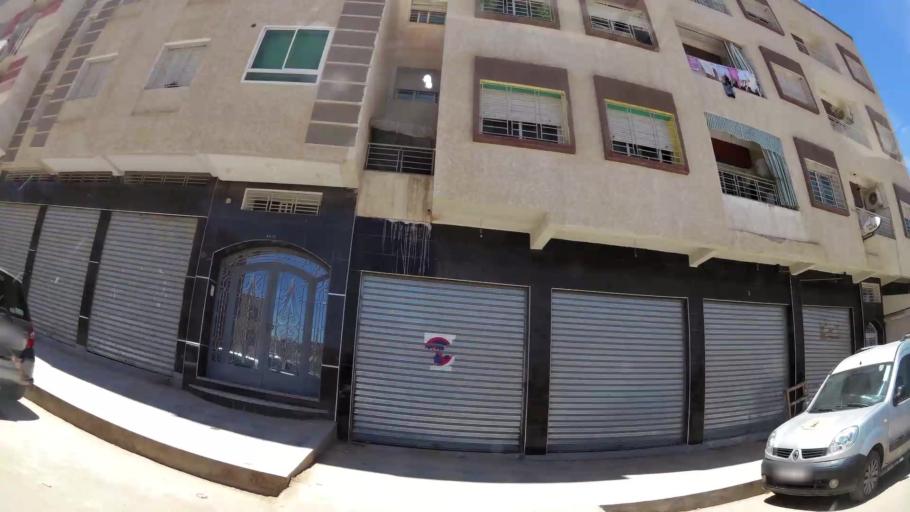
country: MA
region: Meknes-Tafilalet
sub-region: Meknes
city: Meknes
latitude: 33.8577
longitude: -5.5601
